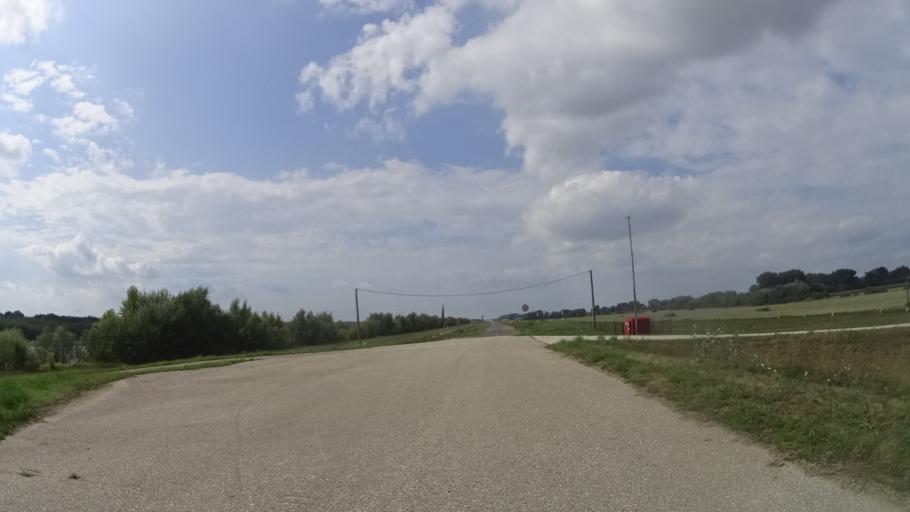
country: SK
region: Trnavsky
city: Gabcikovo
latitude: 47.8248
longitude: 17.6081
